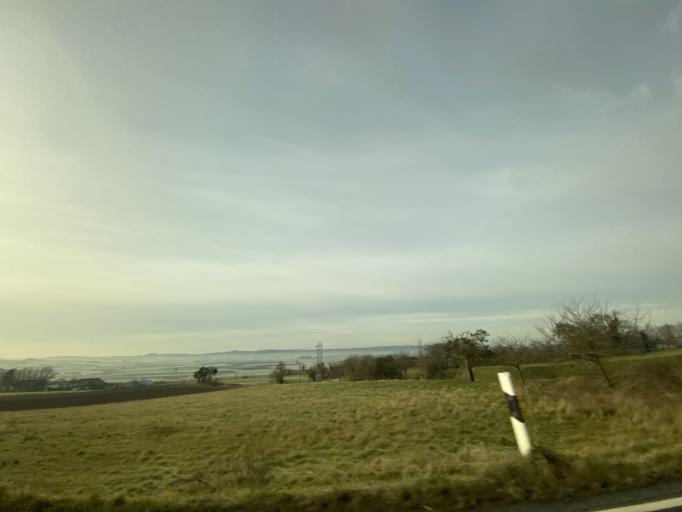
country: DE
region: Hesse
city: Amoneburg
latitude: 50.7944
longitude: 8.9178
